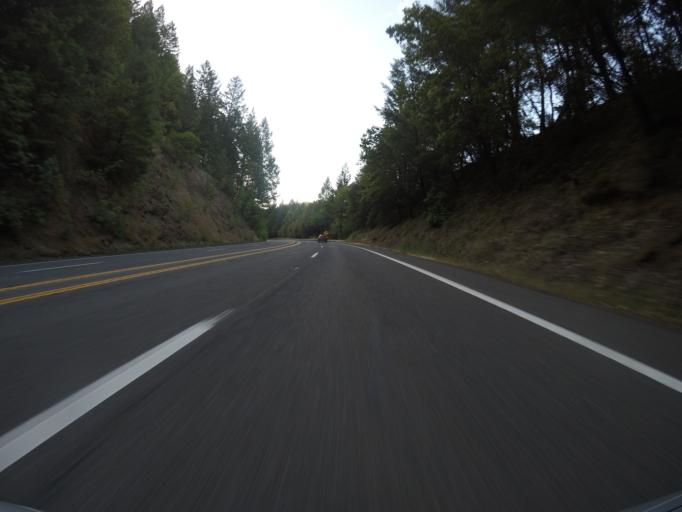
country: US
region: California
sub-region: Mendocino County
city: Brooktrails
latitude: 39.5396
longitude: -123.4176
